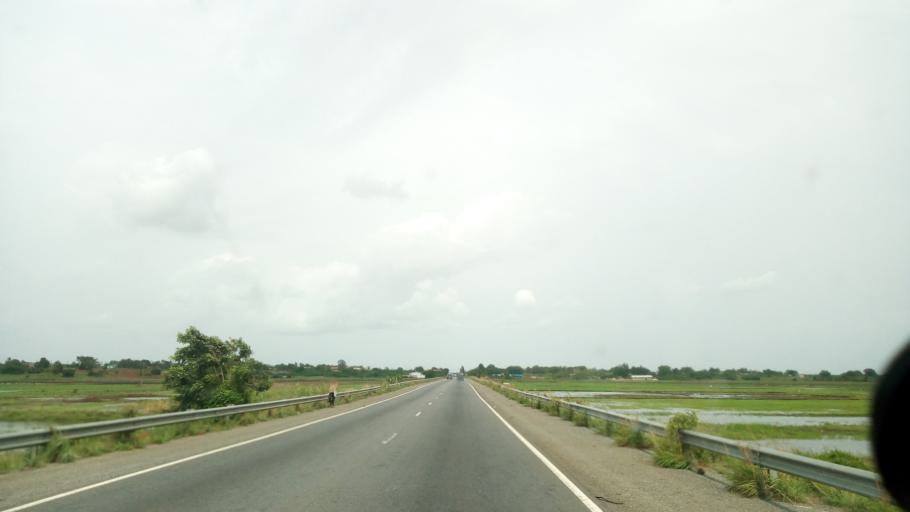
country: GH
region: Volta
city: Keta
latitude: 6.0612
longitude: 0.9360
